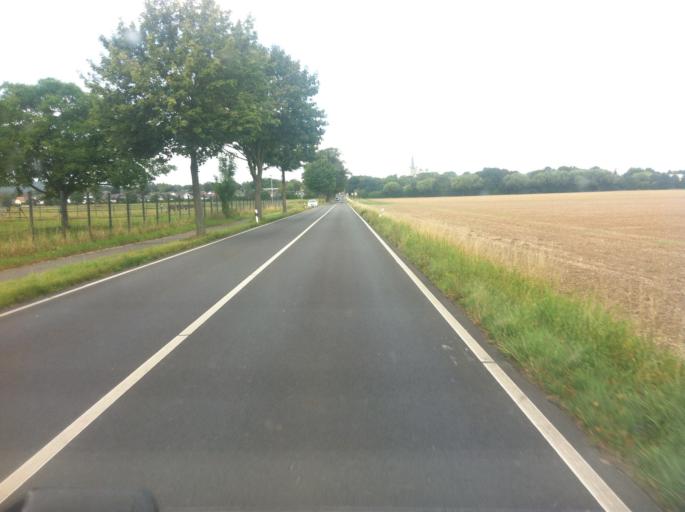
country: DE
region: North Rhine-Westphalia
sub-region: Regierungsbezirk Koln
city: Frechen
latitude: 50.9550
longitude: 6.7992
